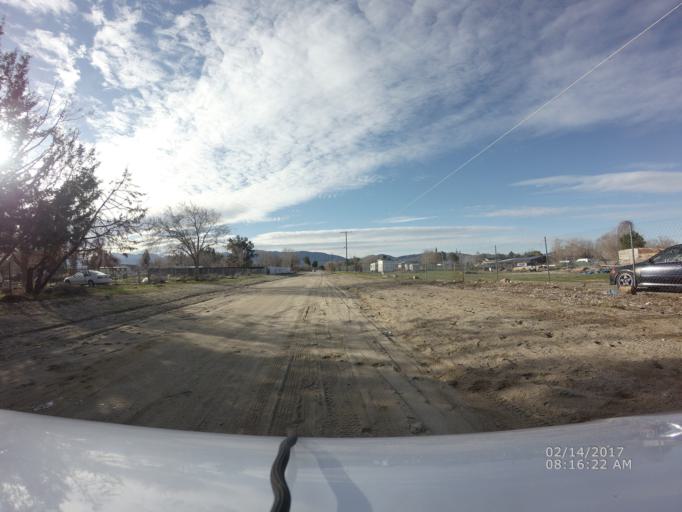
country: US
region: California
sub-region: Los Angeles County
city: Littlerock
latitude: 34.5517
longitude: -117.9538
